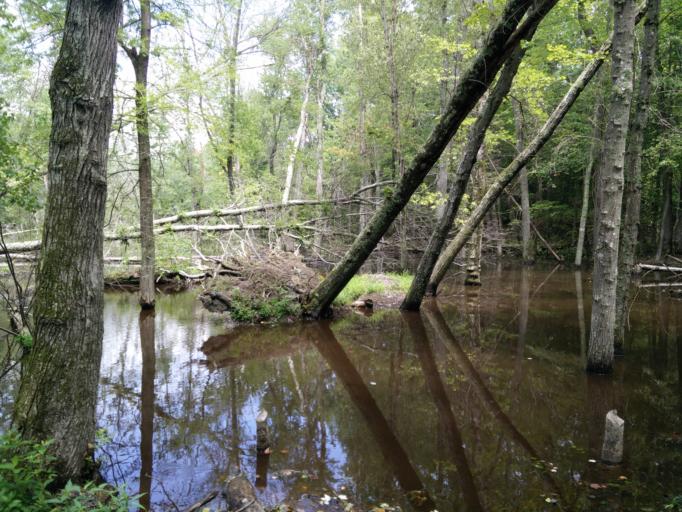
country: US
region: Maryland
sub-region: Prince George's County
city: Baden
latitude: 38.6525
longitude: -76.8190
